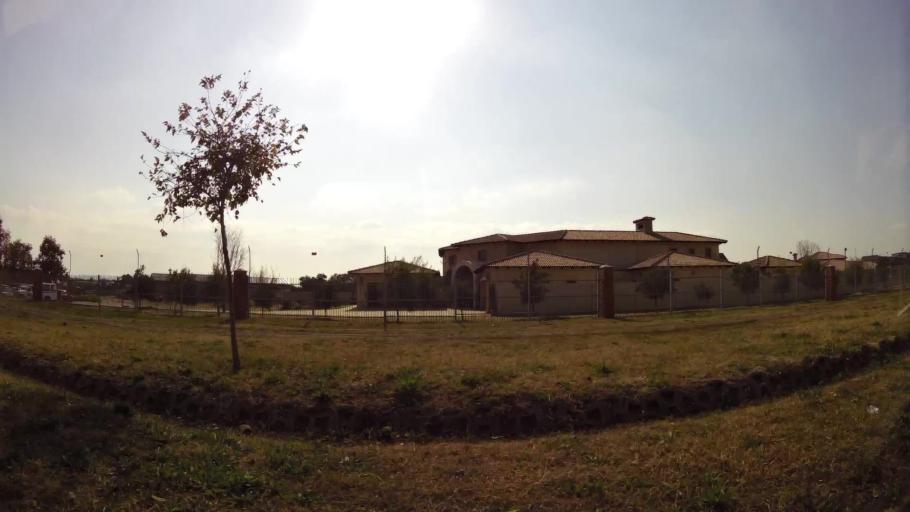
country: ZA
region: Gauteng
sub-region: City of Tshwane Metropolitan Municipality
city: Cullinan
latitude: -25.7792
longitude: 28.3824
